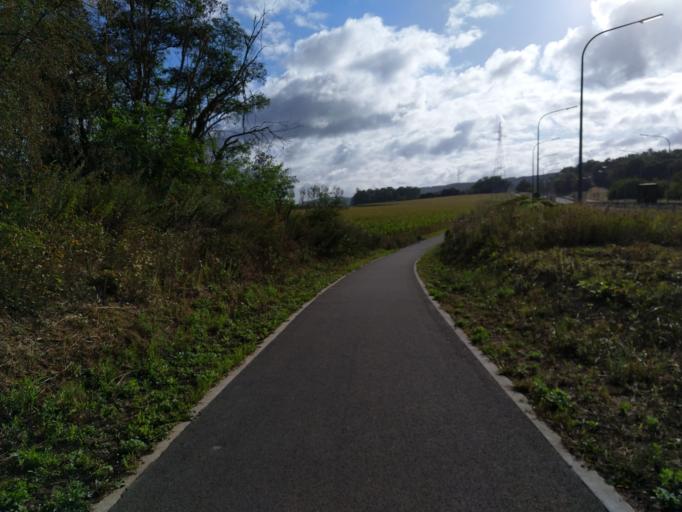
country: BE
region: Wallonia
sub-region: Province de Liege
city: Amay
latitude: 50.5554
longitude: 5.3380
